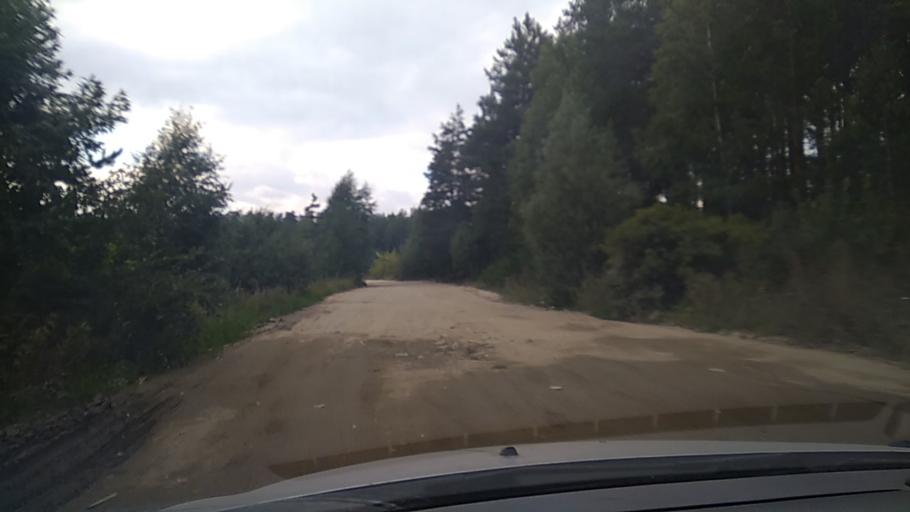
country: RU
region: Chelyabinsk
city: Kyshtym
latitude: 55.6826
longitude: 60.5724
